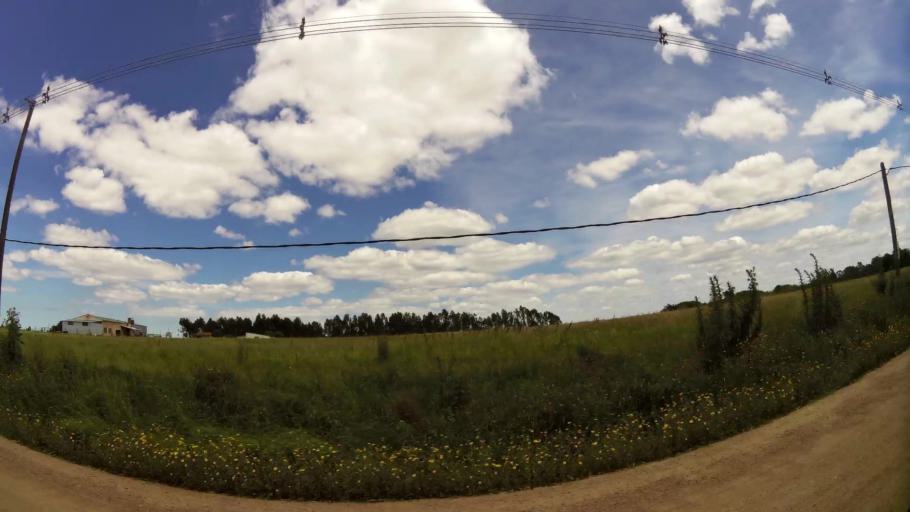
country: UY
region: Canelones
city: Colonia Nicolich
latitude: -34.8185
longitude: -55.9914
